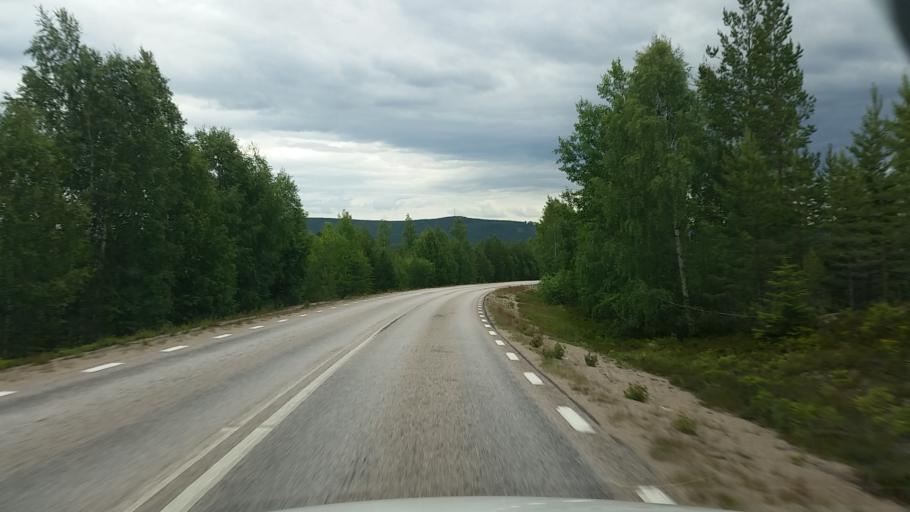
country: SE
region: Gaevleborg
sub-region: Ljusdals Kommun
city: Farila
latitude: 61.9959
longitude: 15.1856
